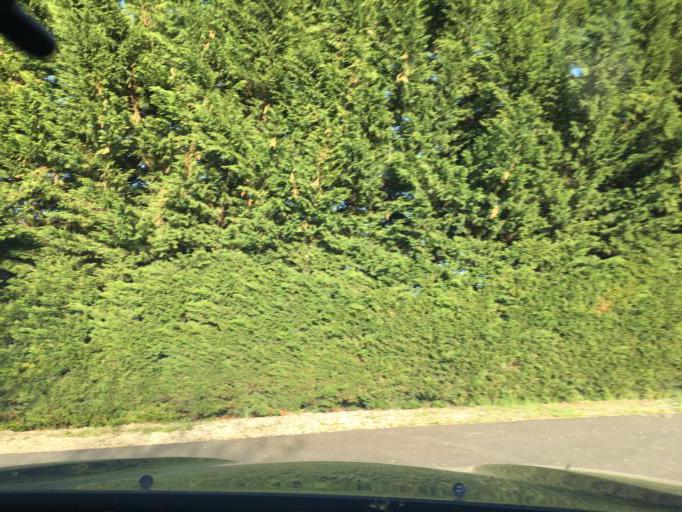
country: FR
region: Centre
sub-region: Departement du Loir-et-Cher
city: Ouzouer-le-Marche
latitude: 47.8953
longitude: 1.5753
